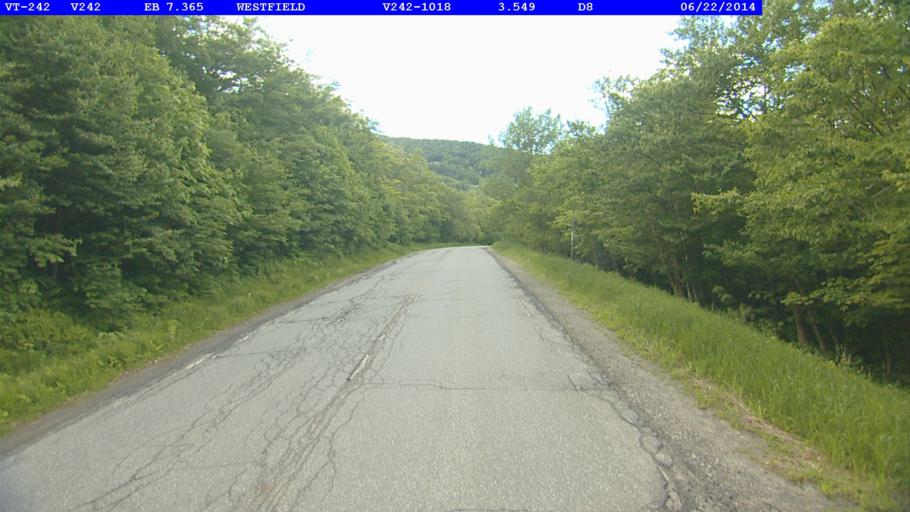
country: US
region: Vermont
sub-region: Franklin County
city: Richford
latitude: 44.9254
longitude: -72.4992
